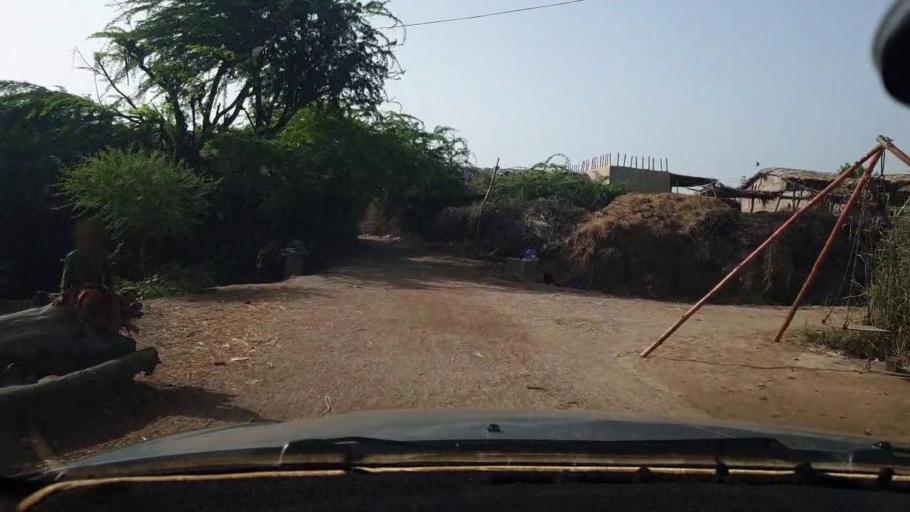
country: PK
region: Sindh
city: Tando Bago
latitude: 24.8180
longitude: 68.8991
